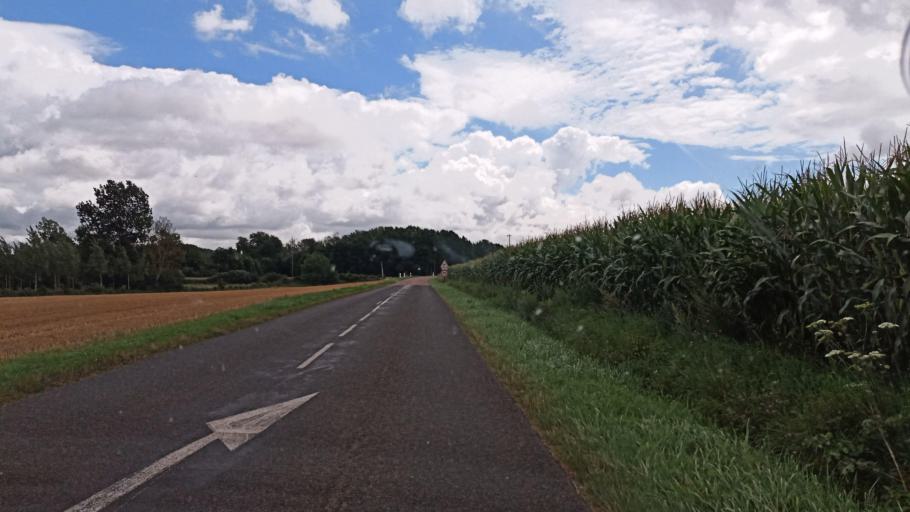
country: FR
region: Ile-de-France
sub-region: Departement de Seine-et-Marne
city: Voulx
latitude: 48.2720
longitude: 2.9982
